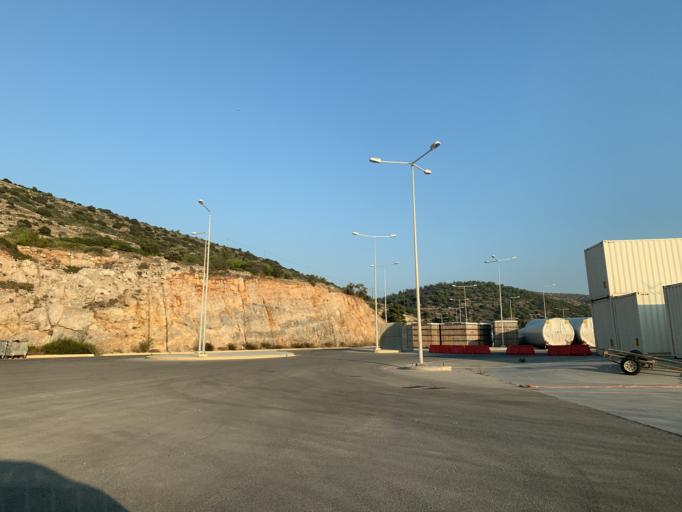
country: GR
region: North Aegean
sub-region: Chios
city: Thymiana
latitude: 38.2921
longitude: 25.9290
